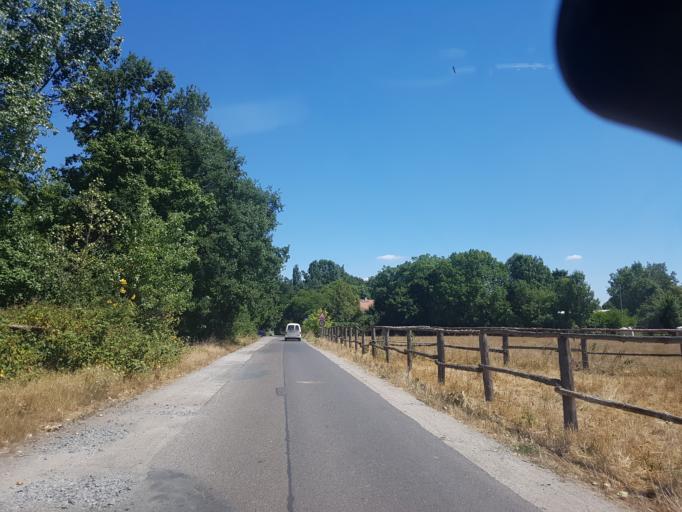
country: DE
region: Brandenburg
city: Teltow
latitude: 52.3860
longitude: 13.2565
